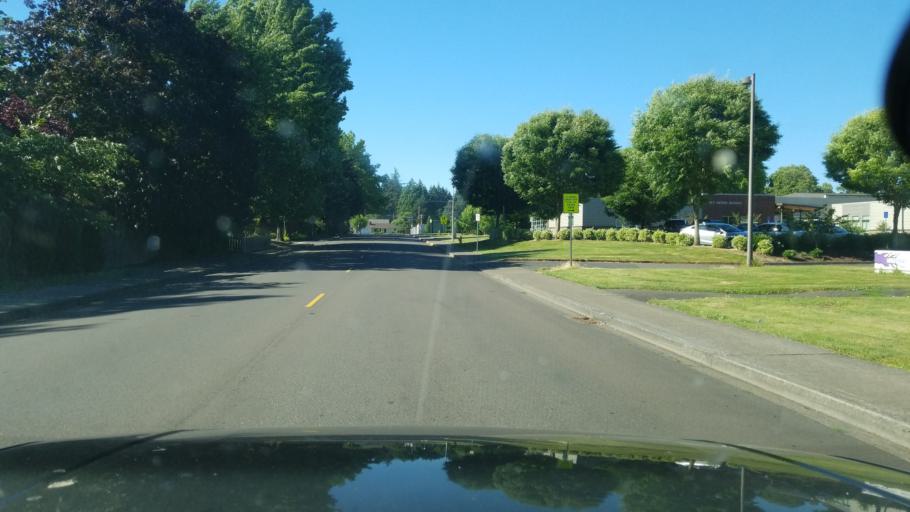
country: US
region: Oregon
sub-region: Yamhill County
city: McMinnville
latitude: 45.2113
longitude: -123.2088
